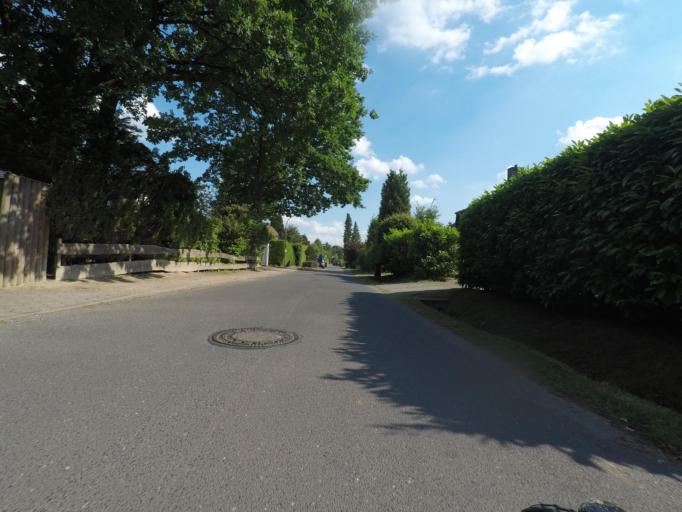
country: DE
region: Hamburg
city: Sasel
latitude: 53.6441
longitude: 10.1065
